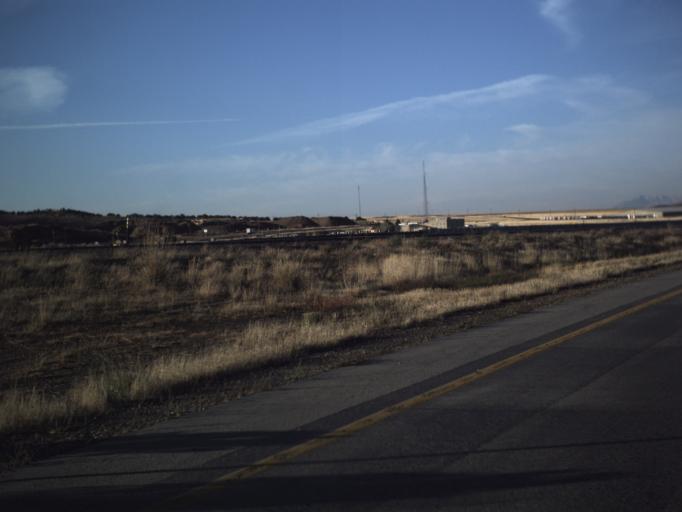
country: US
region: Utah
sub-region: Juab County
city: Nephi
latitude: 39.6813
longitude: -111.8403
